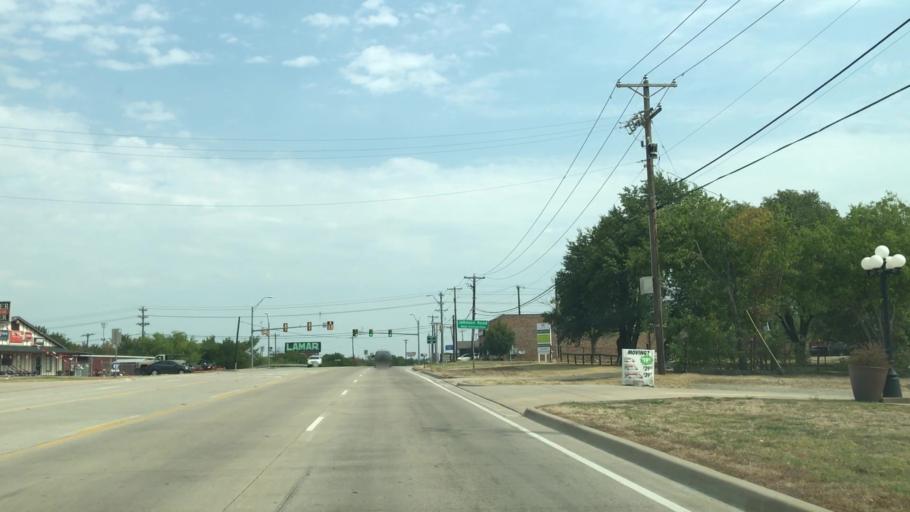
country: US
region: Texas
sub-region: Tarrant County
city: Keller
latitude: 32.9404
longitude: -97.2535
